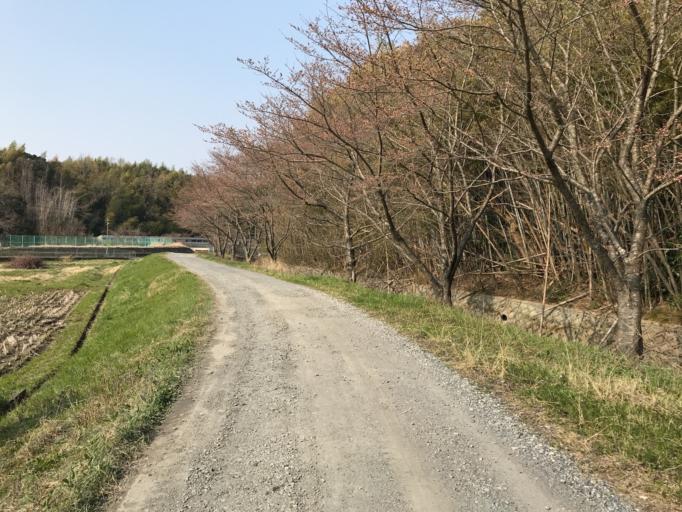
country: JP
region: Kyoto
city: Tanabe
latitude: 34.7914
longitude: 135.7821
